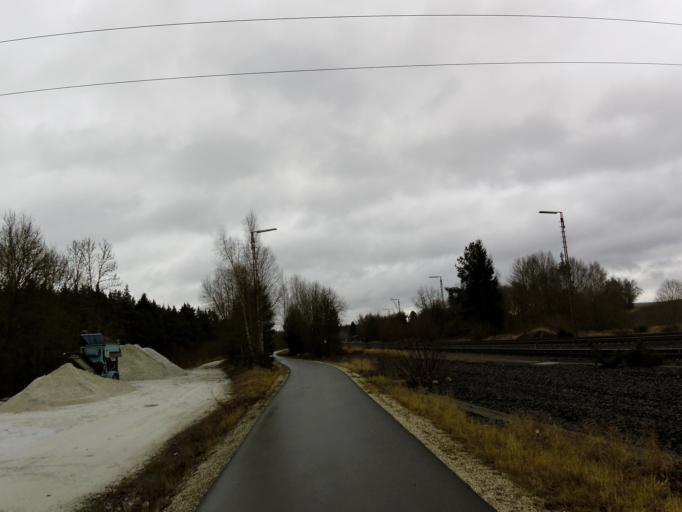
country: DE
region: Bavaria
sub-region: Upper Franconia
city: Wunsiedel
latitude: 50.0541
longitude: 12.0314
